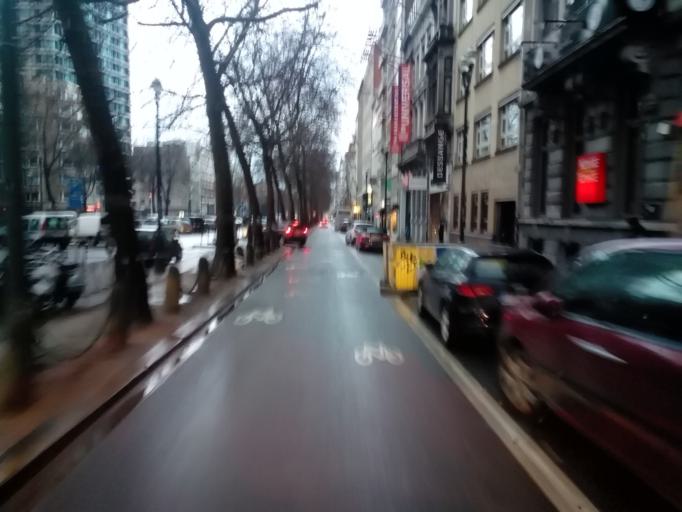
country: BE
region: Brussels Capital
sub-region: Bruxelles-Capitale
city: Brussels
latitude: 50.8275
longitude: 4.3639
